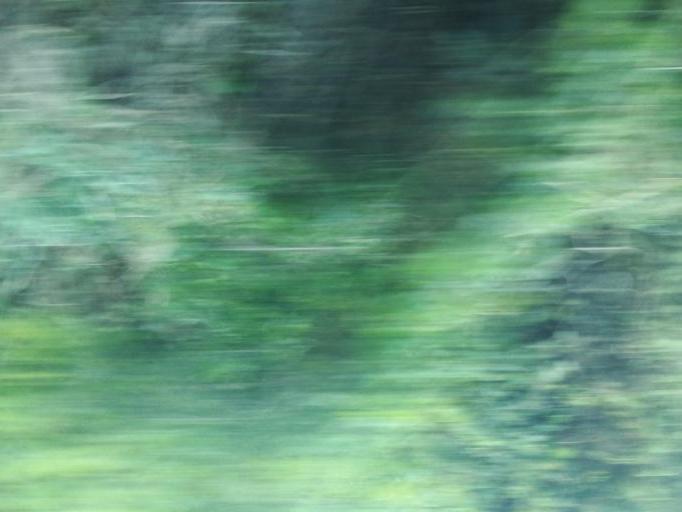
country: BR
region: Minas Gerais
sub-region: Ipaba
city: Ipaba
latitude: -19.4639
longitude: -42.4553
